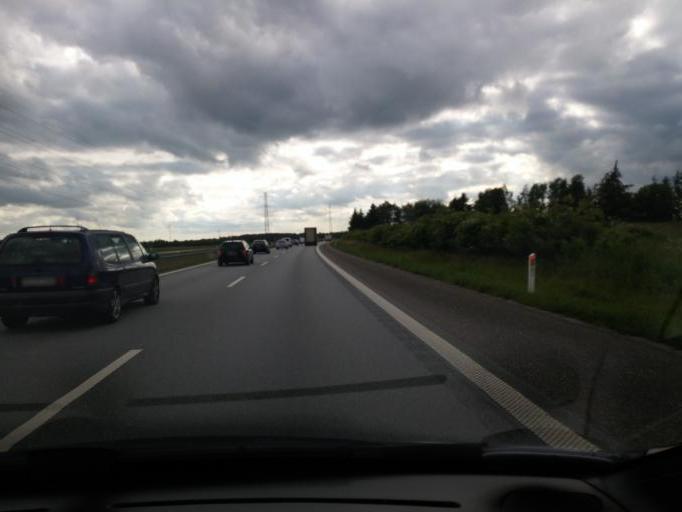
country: DK
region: Zealand
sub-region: Ringsted Kommune
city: Ringsted
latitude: 55.4536
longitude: 11.8692
